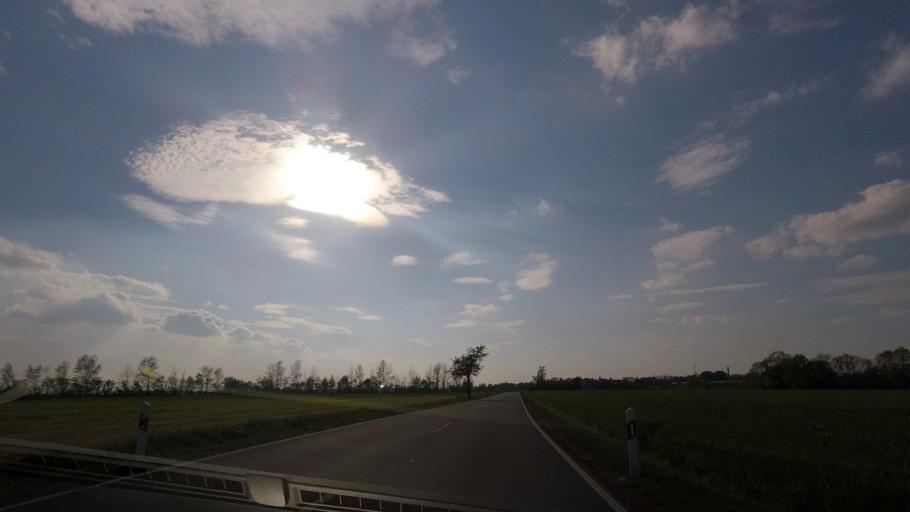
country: DE
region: Brandenburg
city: Dahme
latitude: 51.8616
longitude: 13.4503
